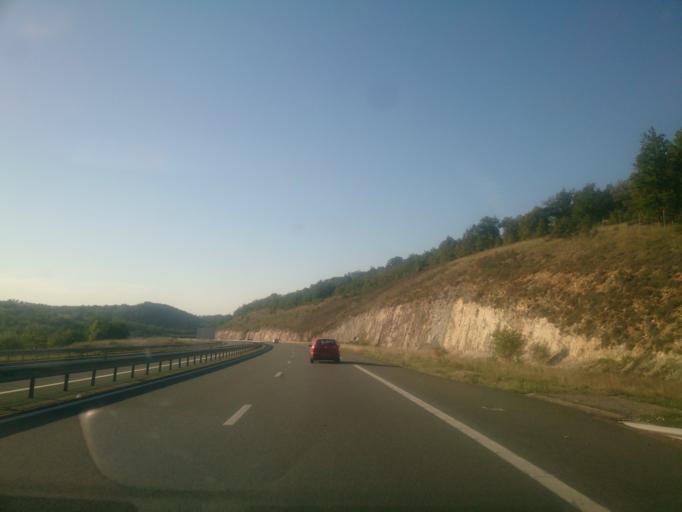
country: FR
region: Midi-Pyrenees
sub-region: Departement du Lot
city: Le Vigan
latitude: 44.7406
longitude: 1.5534
